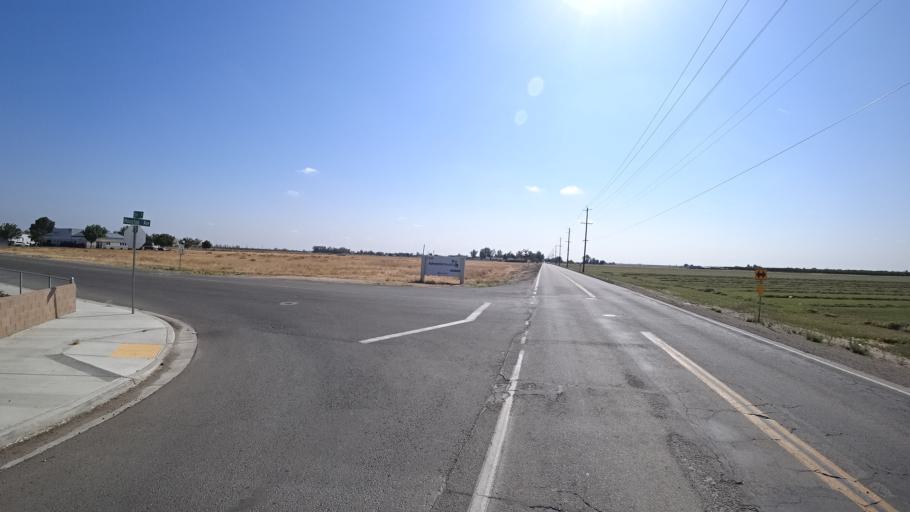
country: US
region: California
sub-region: Kings County
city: Home Garden
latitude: 36.2987
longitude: -119.6314
